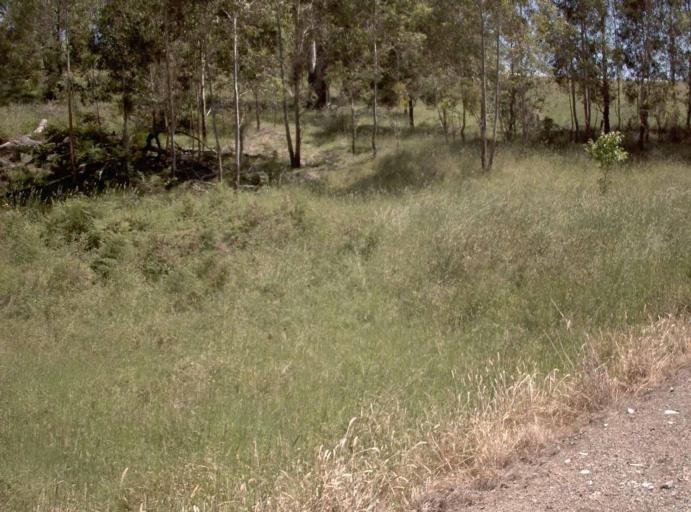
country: AU
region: Victoria
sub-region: East Gippsland
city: Lakes Entrance
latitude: -37.3974
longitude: 148.2132
